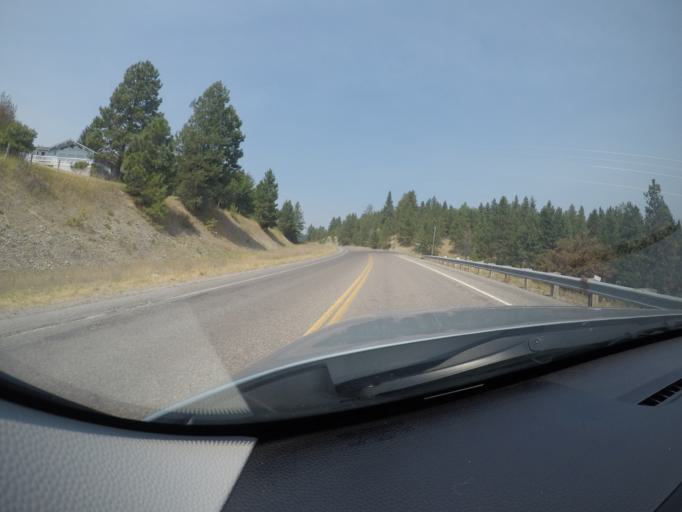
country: US
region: Montana
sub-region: Lake County
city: Polson
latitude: 47.7619
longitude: -114.1642
